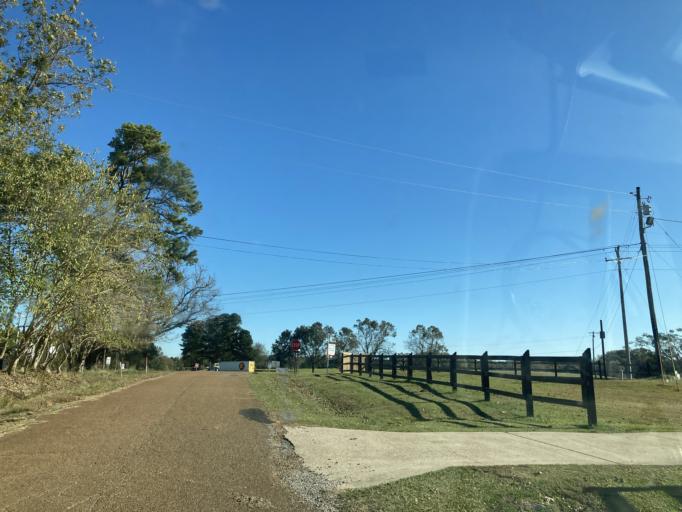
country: US
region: Mississippi
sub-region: Madison County
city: Kearney Park
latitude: 32.7171
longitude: -90.3745
